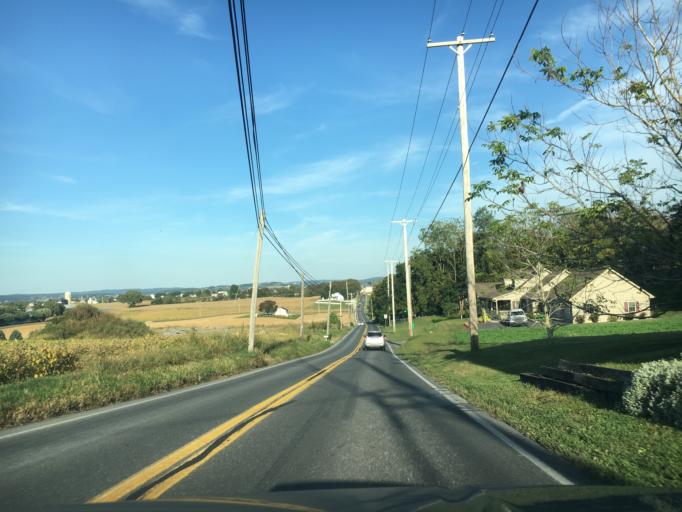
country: US
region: Pennsylvania
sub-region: Lancaster County
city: Ephrata
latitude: 40.1330
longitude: -76.1416
